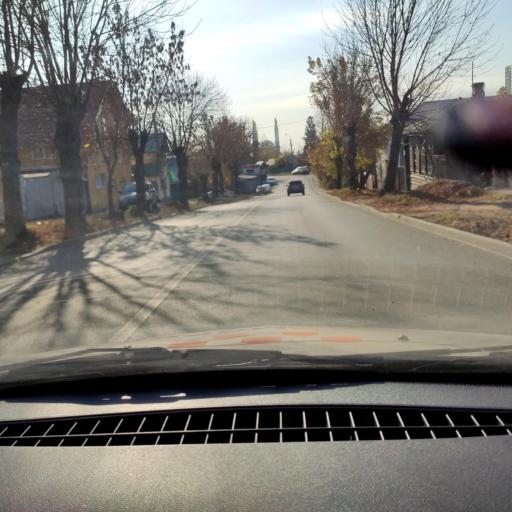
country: RU
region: Bashkortostan
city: Ufa
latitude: 54.7241
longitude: 55.9690
